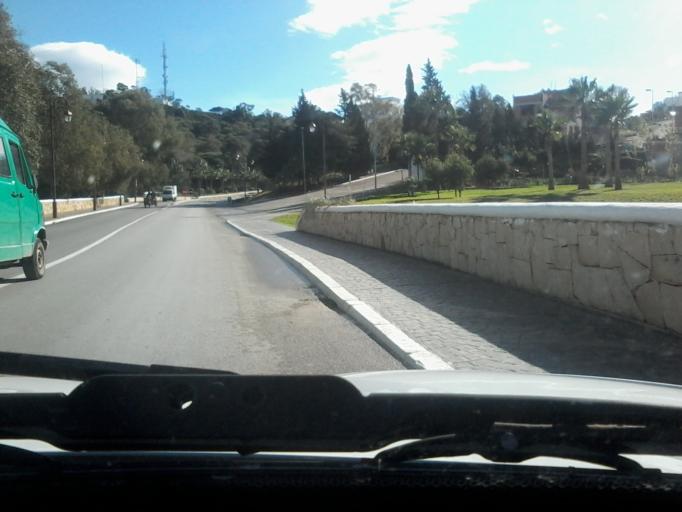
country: MA
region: Tanger-Tetouan
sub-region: Tetouan
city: Martil
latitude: 35.6765
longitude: -5.3232
